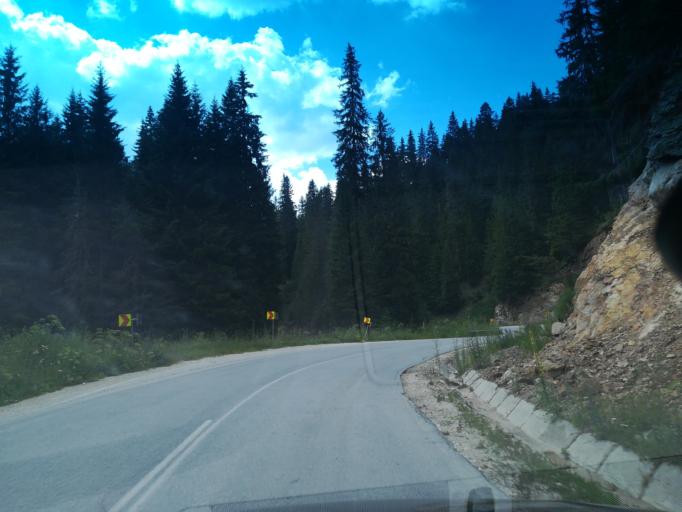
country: BG
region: Smolyan
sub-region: Obshtina Chepelare
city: Chepelare
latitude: 41.6614
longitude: 24.6727
